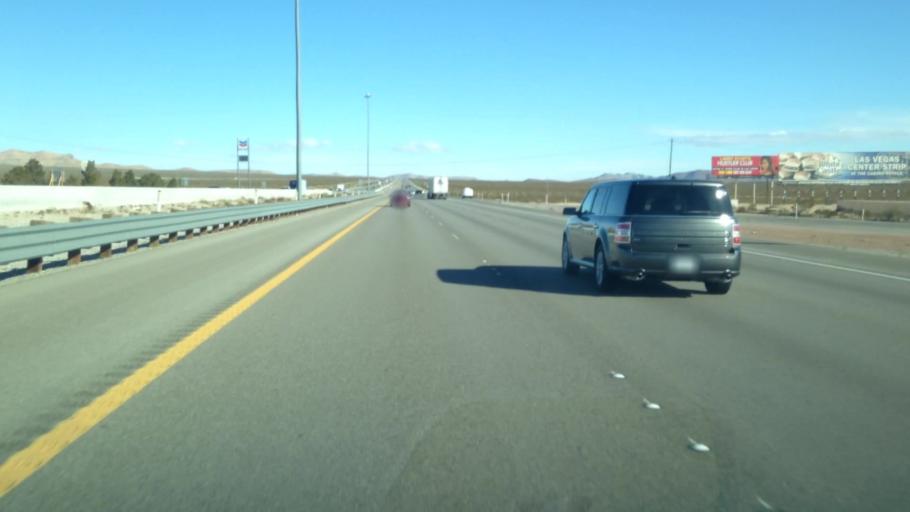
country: US
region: Nevada
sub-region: Clark County
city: Enterprise
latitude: 35.7826
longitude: -115.3265
